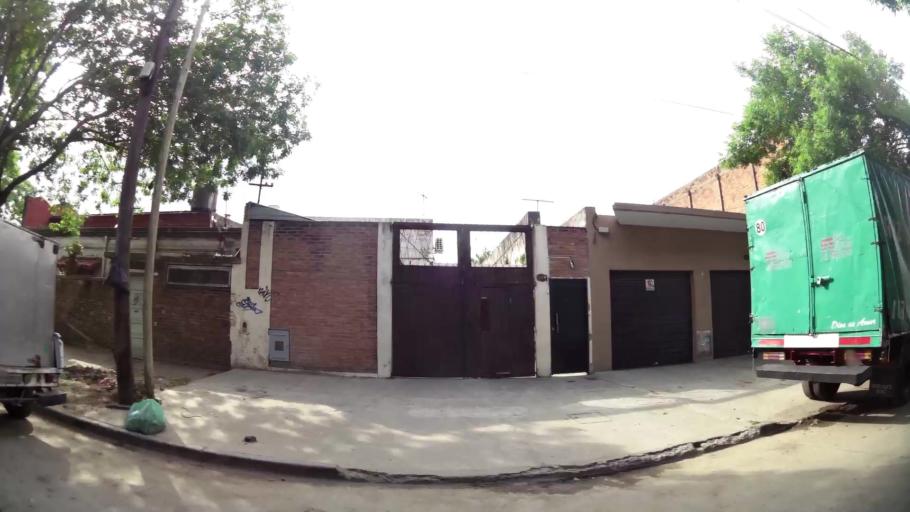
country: AR
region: Buenos Aires
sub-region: Partido de Lanus
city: Lanus
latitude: -34.6907
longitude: -58.3800
